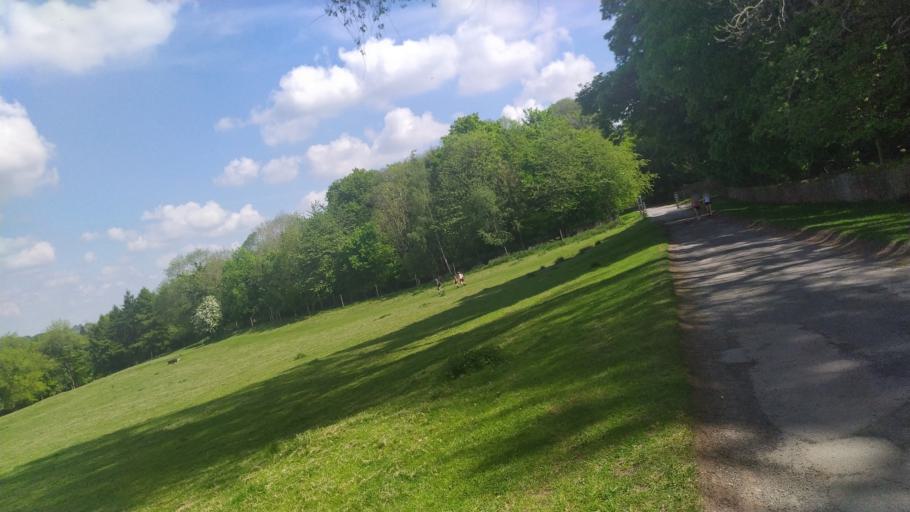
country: GB
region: England
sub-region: North Yorkshire
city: Pannal
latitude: 53.9017
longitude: -1.5253
